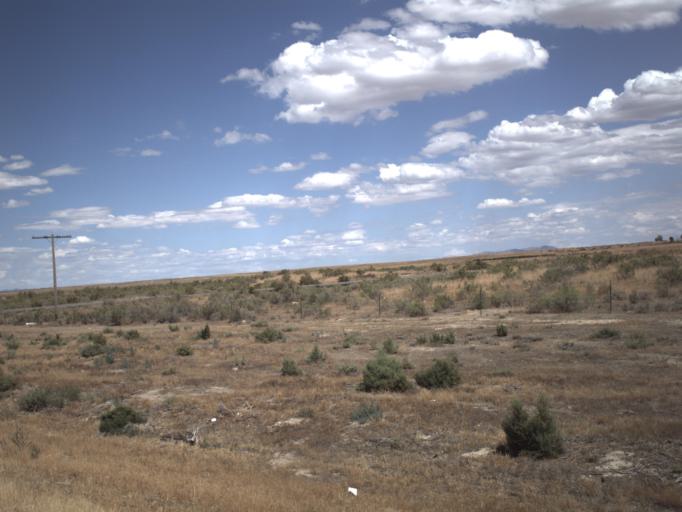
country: US
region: Utah
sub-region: Millard County
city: Delta
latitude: 39.3253
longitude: -112.4843
